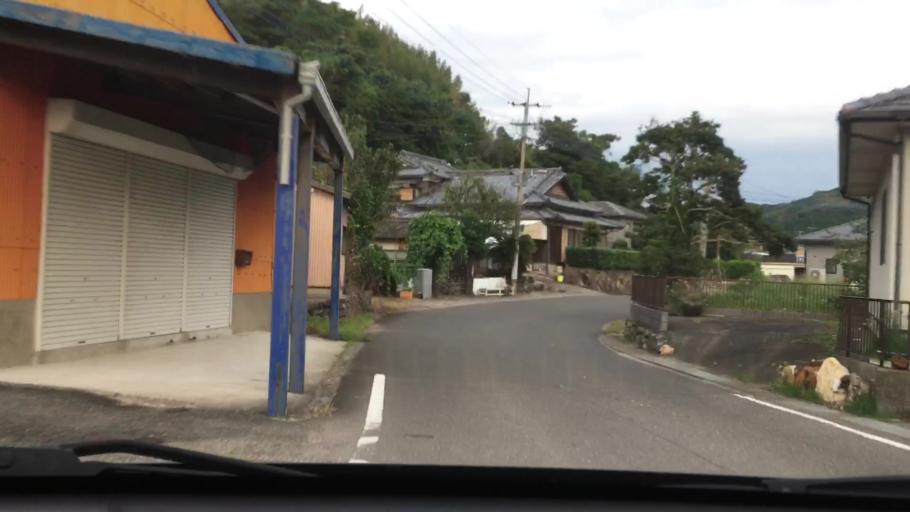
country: JP
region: Nagasaki
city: Sasebo
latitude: 33.0011
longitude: 129.7651
